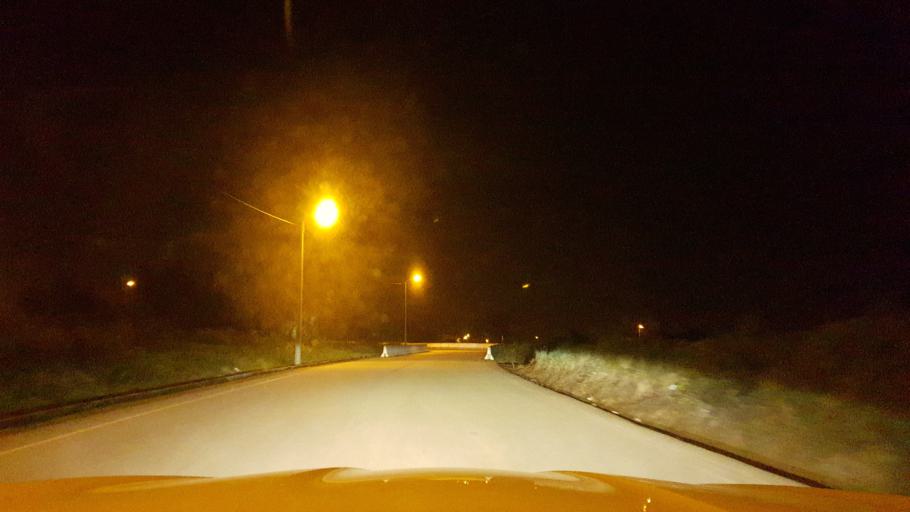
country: PT
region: Porto
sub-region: Matosinhos
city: Senhora da Hora
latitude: 41.2099
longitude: -8.6431
